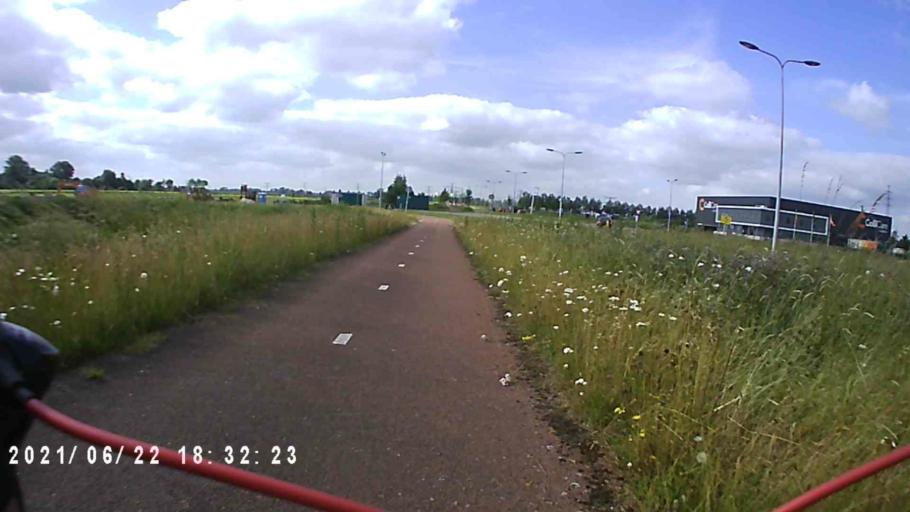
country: NL
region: Groningen
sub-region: Gemeente Zuidhorn
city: Aduard
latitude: 53.2046
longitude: 6.4724
